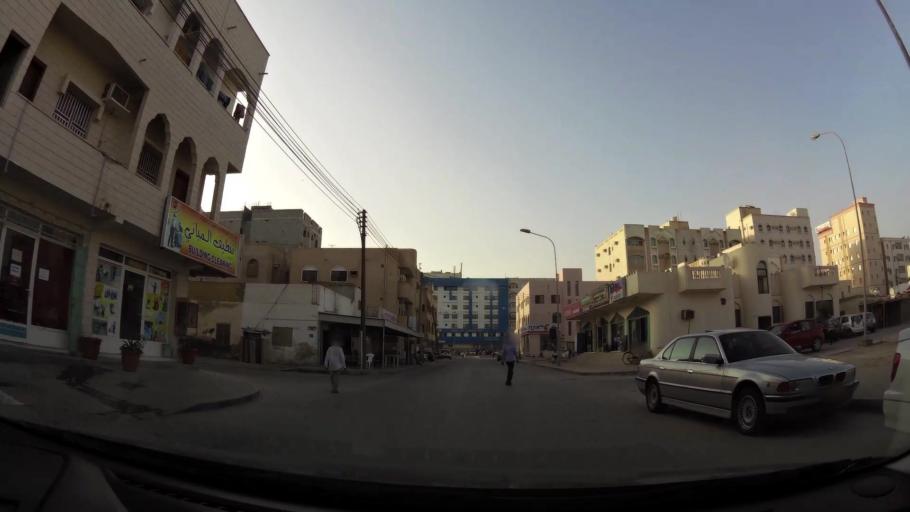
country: OM
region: Zufar
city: Salalah
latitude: 17.0161
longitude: 54.0996
